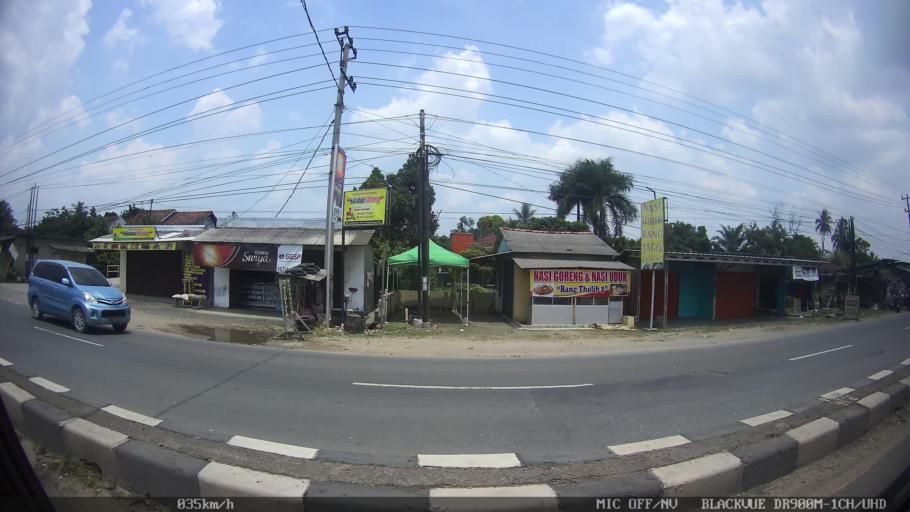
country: ID
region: Lampung
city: Natar
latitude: -5.2848
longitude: 105.1910
